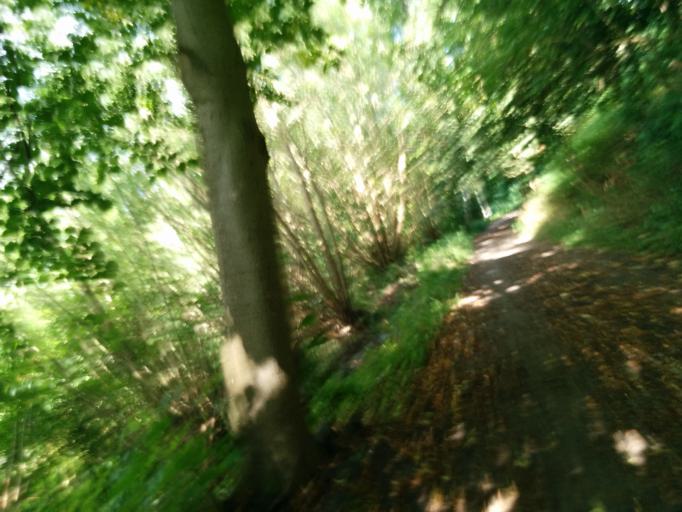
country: DE
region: Schleswig-Holstein
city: Wedel
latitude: 53.5657
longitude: 9.7334
